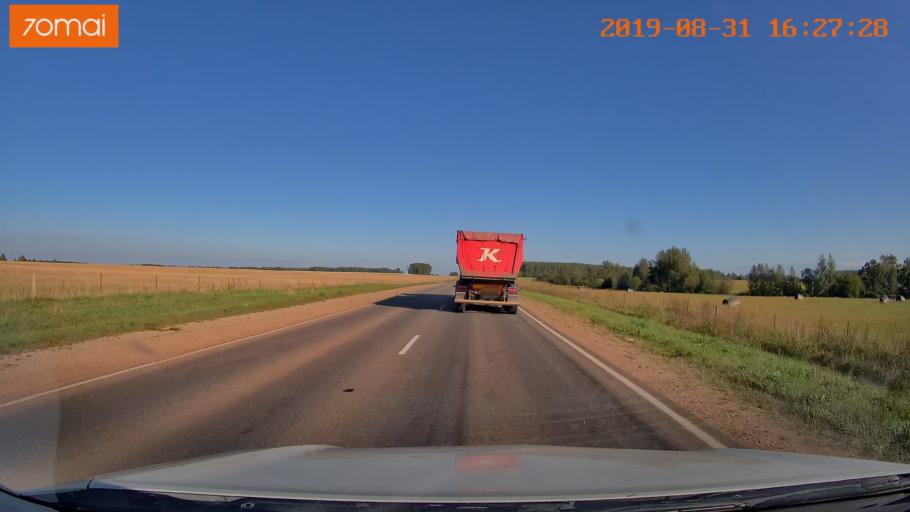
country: RU
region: Kaluga
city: Babynino
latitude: 54.5138
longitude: 35.7615
